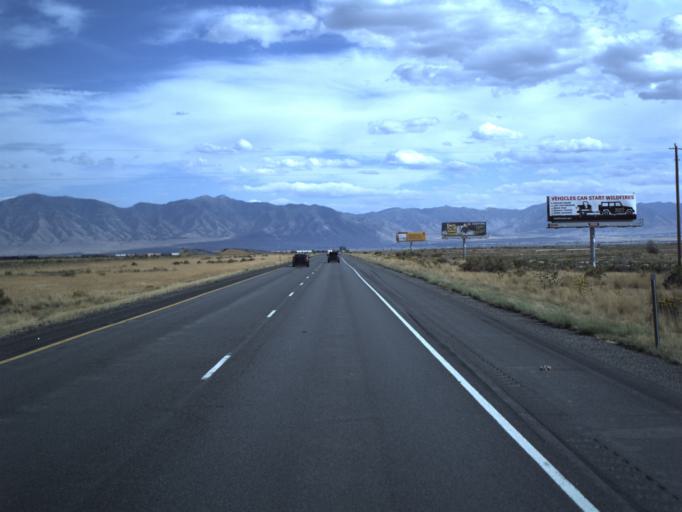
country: US
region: Utah
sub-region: Tooele County
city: Grantsville
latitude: 40.6886
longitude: -112.4575
